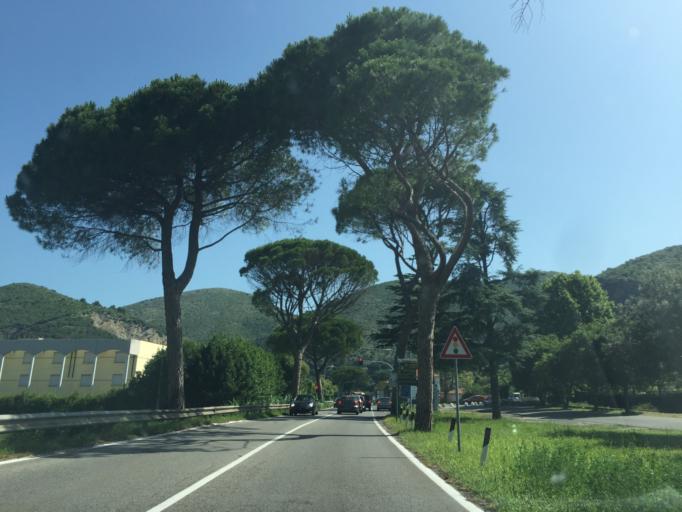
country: IT
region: Tuscany
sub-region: Province of Pisa
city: San Giuliano Terme
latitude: 43.7587
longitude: 10.4409
